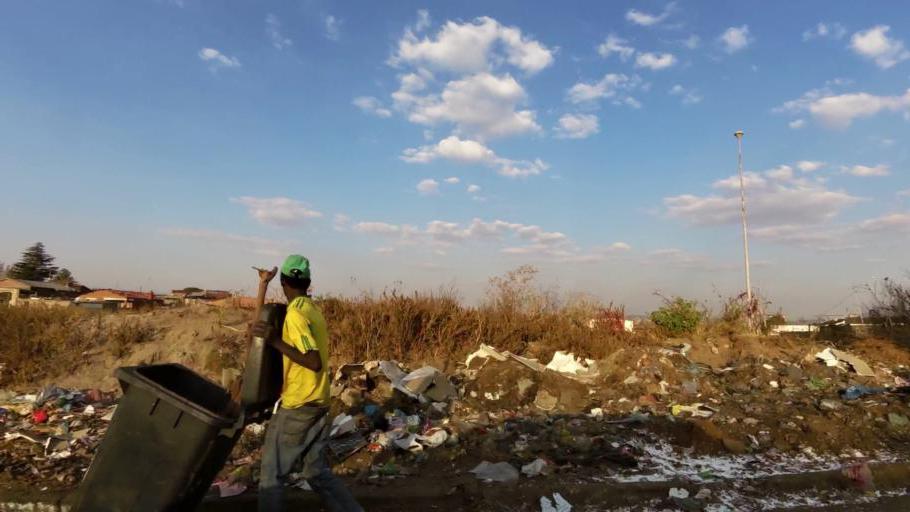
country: ZA
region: Gauteng
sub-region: City of Johannesburg Metropolitan Municipality
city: Soweto
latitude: -26.2273
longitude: 27.9055
